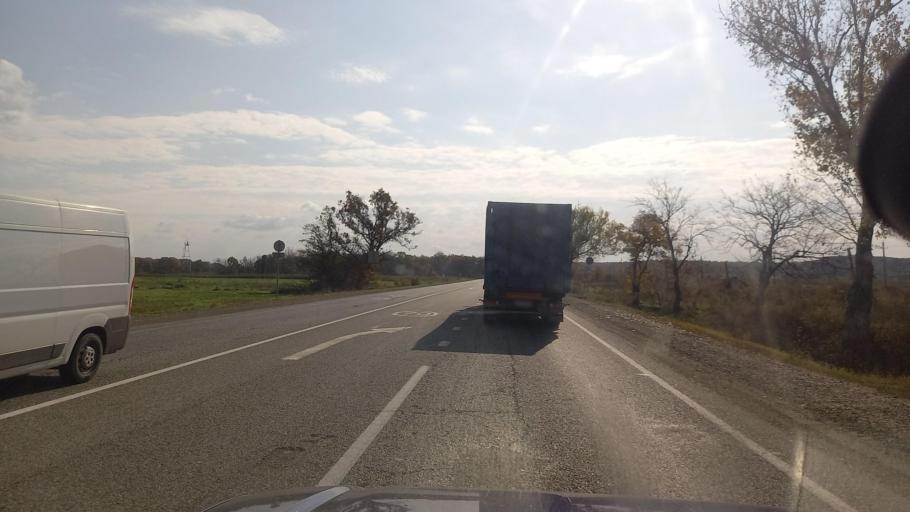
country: RU
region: Krasnodarskiy
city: Novoukrainskiy
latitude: 44.8835
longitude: 38.0902
